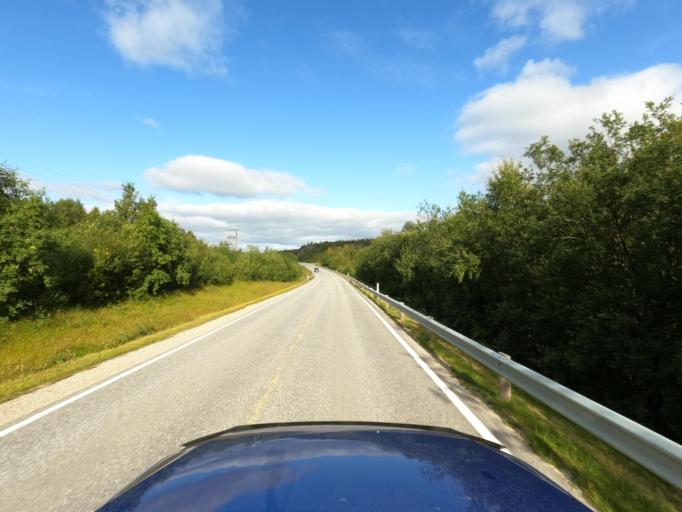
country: NO
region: Finnmark Fylke
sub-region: Porsanger
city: Lakselv
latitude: 70.0100
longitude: 24.9640
